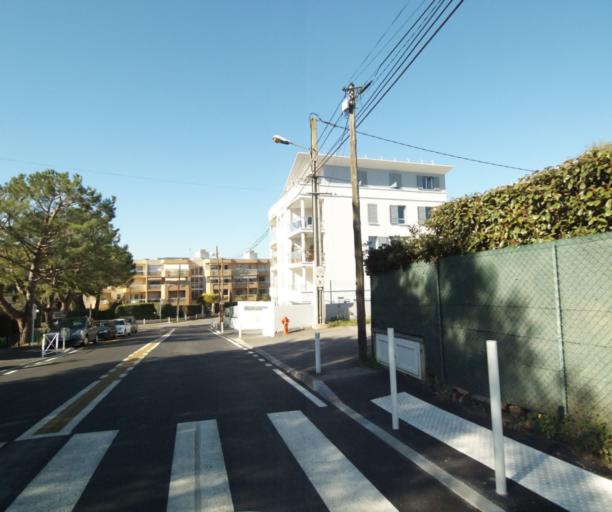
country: FR
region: Provence-Alpes-Cote d'Azur
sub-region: Departement des Alpes-Maritimes
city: Biot
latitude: 43.5974
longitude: 7.0951
